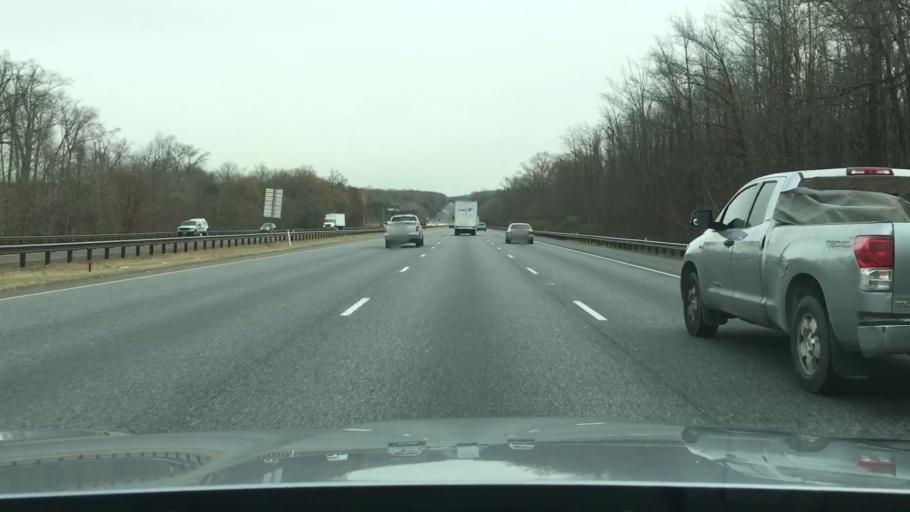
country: US
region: Maryland
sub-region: Prince George's County
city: Bowie
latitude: 38.9554
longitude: -76.7030
